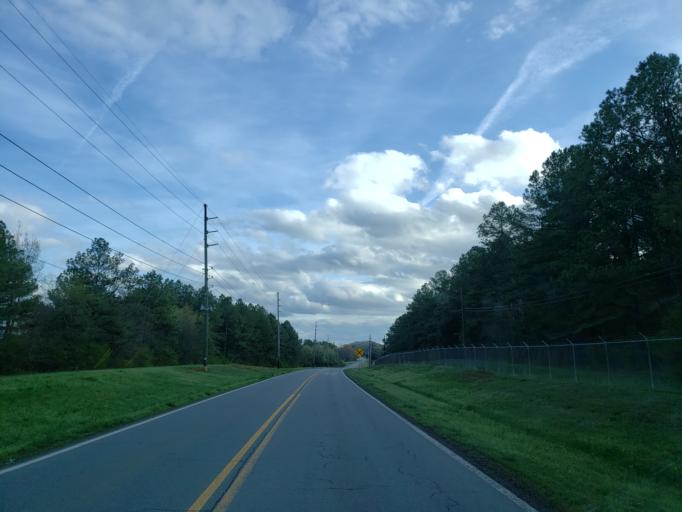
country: US
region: Georgia
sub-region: Bartow County
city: Cartersville
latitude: 34.2354
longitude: -84.8053
